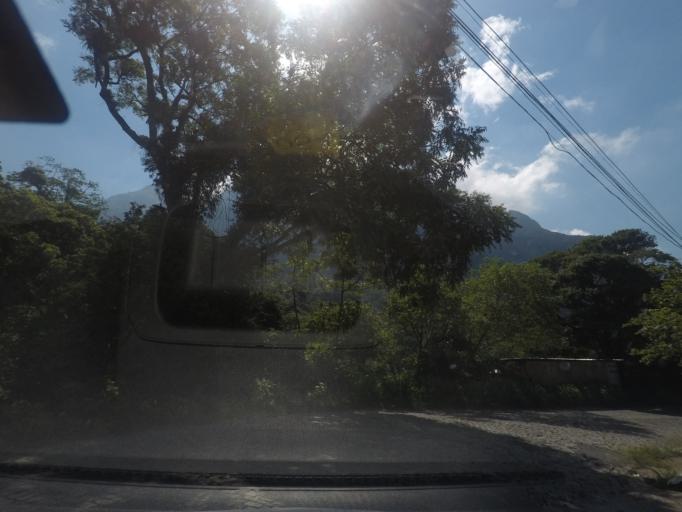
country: BR
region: Rio de Janeiro
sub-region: Petropolis
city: Petropolis
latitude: -22.5467
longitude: -43.1789
